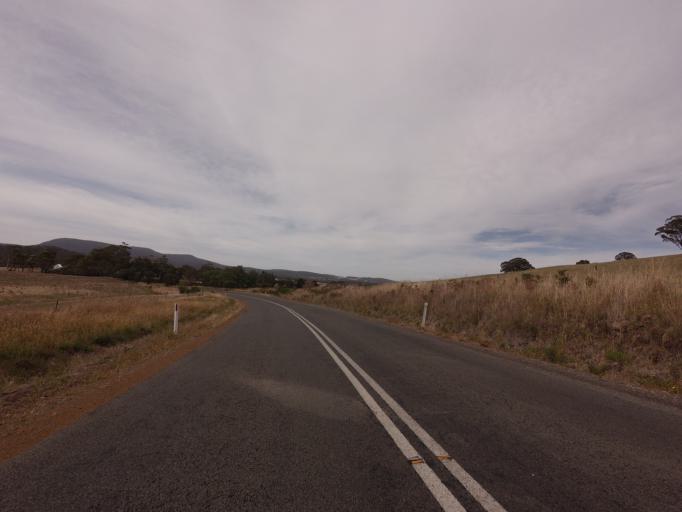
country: AU
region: Tasmania
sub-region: Sorell
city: Sorell
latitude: -42.4238
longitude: 147.4647
